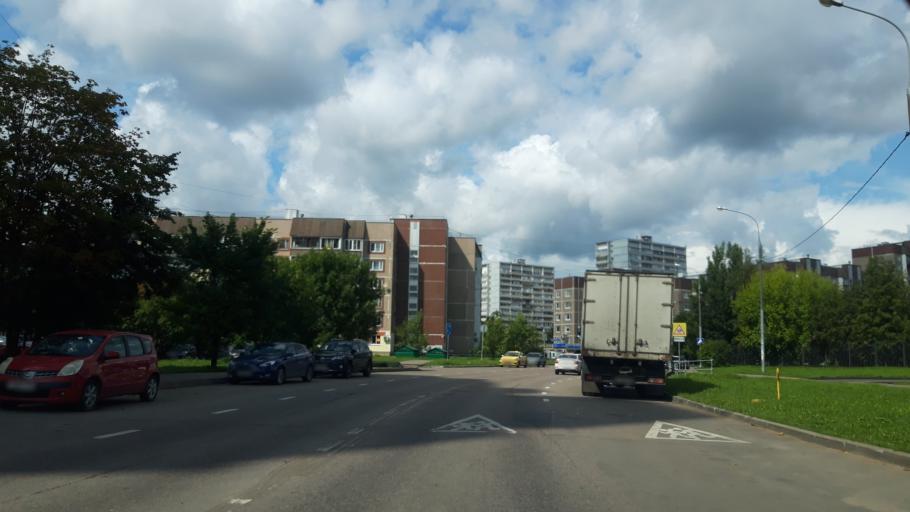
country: RU
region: Moscow
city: Zelenograd
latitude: 55.9787
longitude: 37.1670
